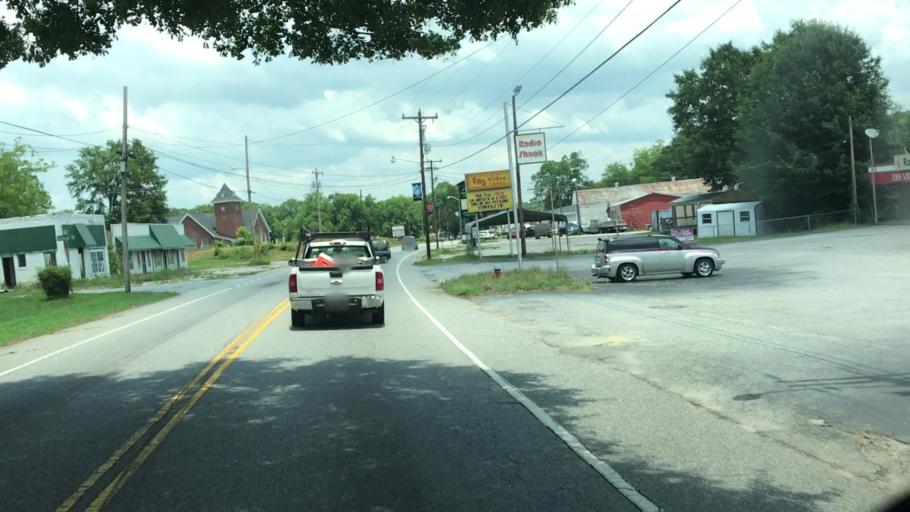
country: US
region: South Carolina
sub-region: Anderson County
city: Williamston
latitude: 34.6266
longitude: -82.4706
